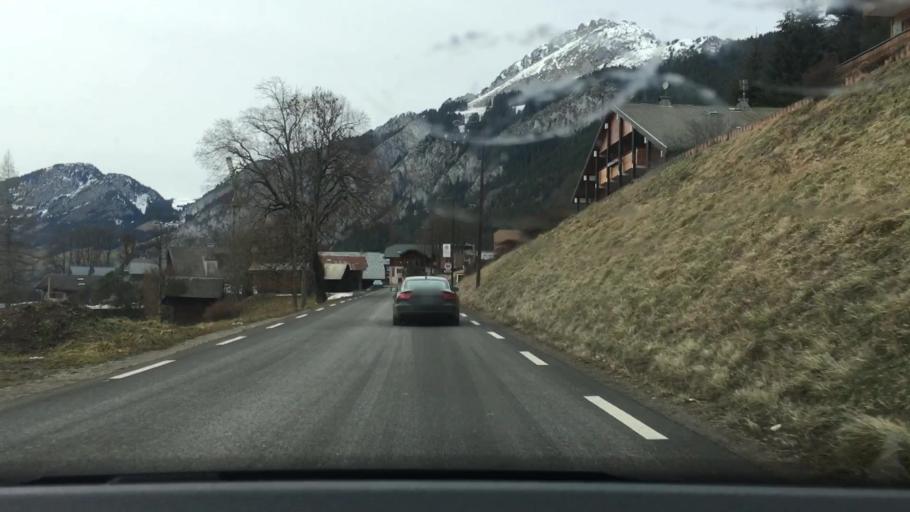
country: FR
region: Rhone-Alpes
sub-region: Departement de la Haute-Savoie
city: Chatel
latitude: 46.2928
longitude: 6.7980
